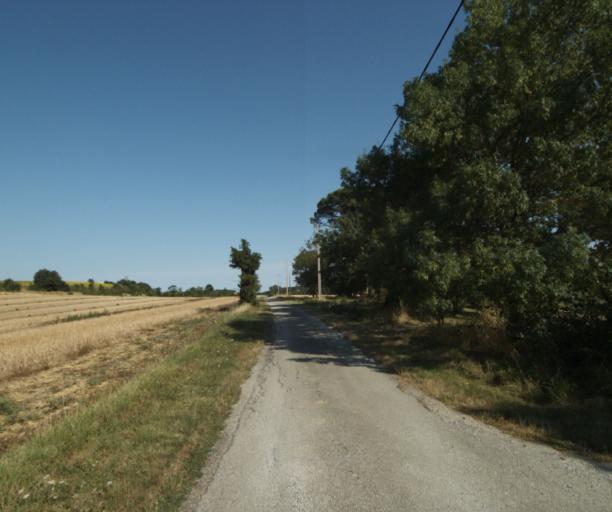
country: FR
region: Midi-Pyrenees
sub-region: Departement de la Haute-Garonne
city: Avignonet-Lauragais
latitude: 43.4199
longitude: 1.8144
